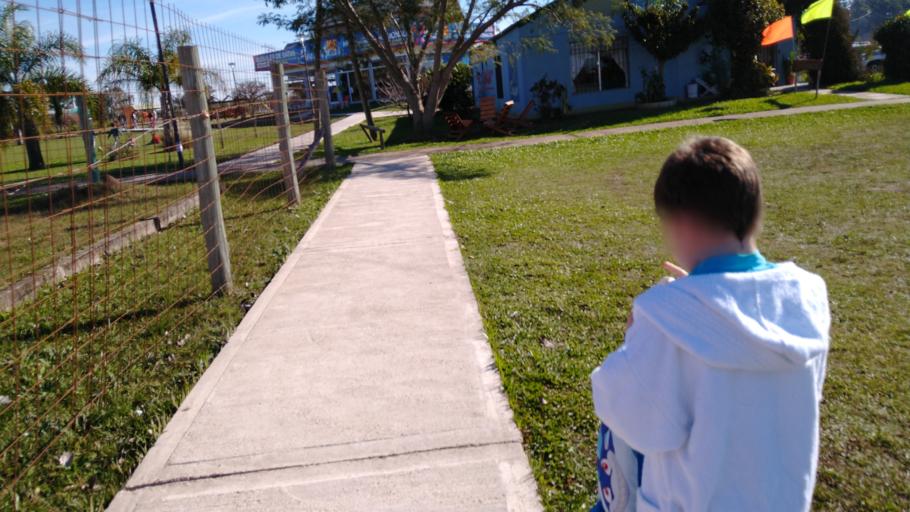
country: AR
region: Entre Rios
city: Chajari
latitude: -30.7442
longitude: -58.0121
